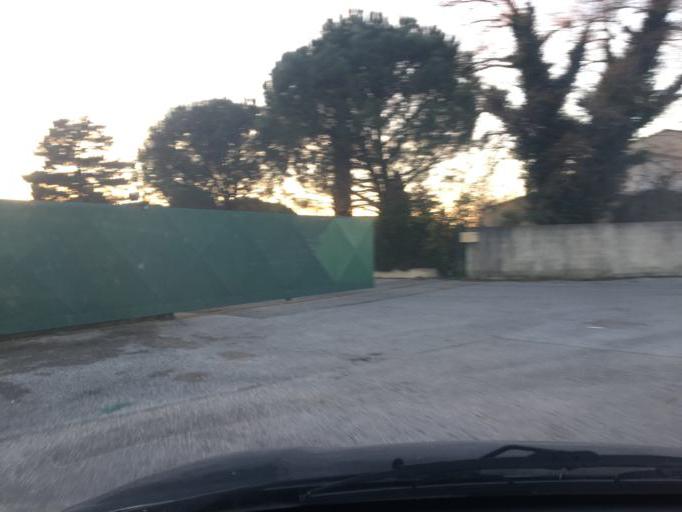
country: FR
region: Provence-Alpes-Cote d'Azur
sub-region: Departement des Bouches-du-Rhone
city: Mallemort
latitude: 43.7362
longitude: 5.1755
